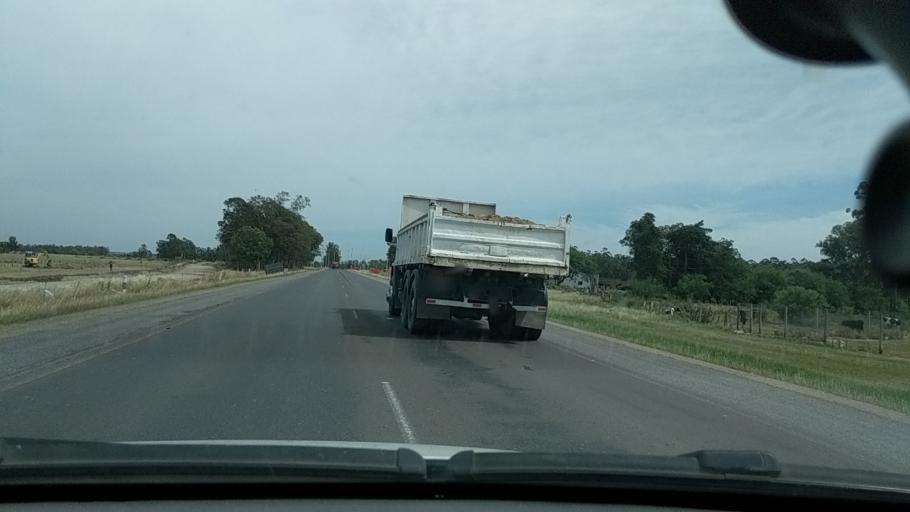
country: UY
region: Durazno
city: Durazno
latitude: -33.4165
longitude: -56.5075
